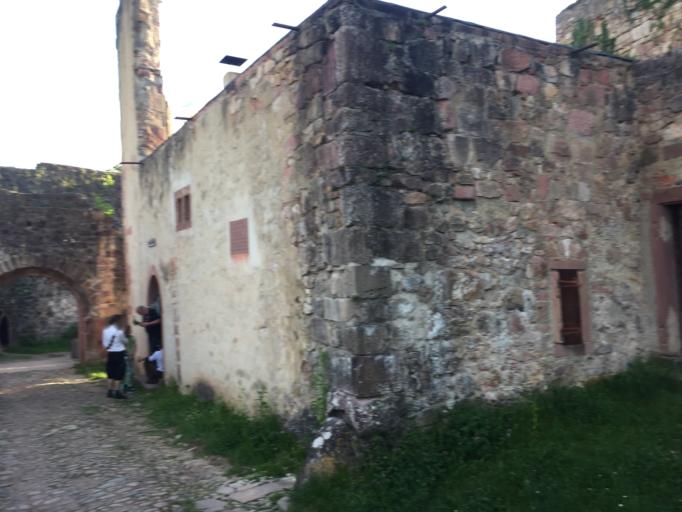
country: DE
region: Baden-Wuerttemberg
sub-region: Freiburg Region
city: Sexau
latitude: 48.1167
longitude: 7.9006
